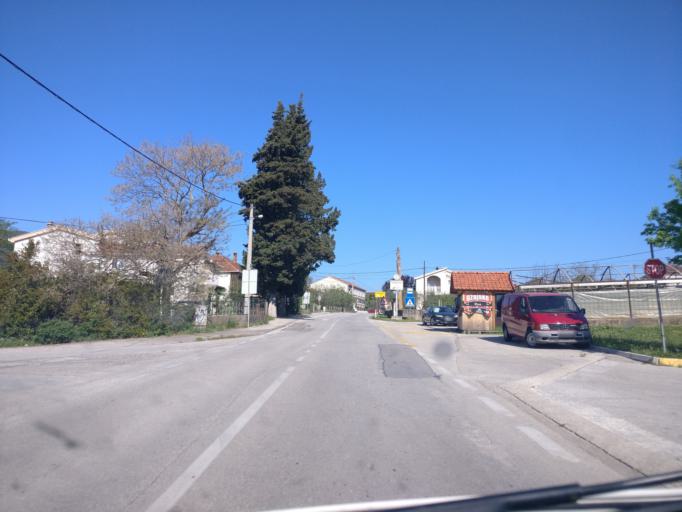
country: BA
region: Federation of Bosnia and Herzegovina
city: Capljina
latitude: 43.1214
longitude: 17.6856
